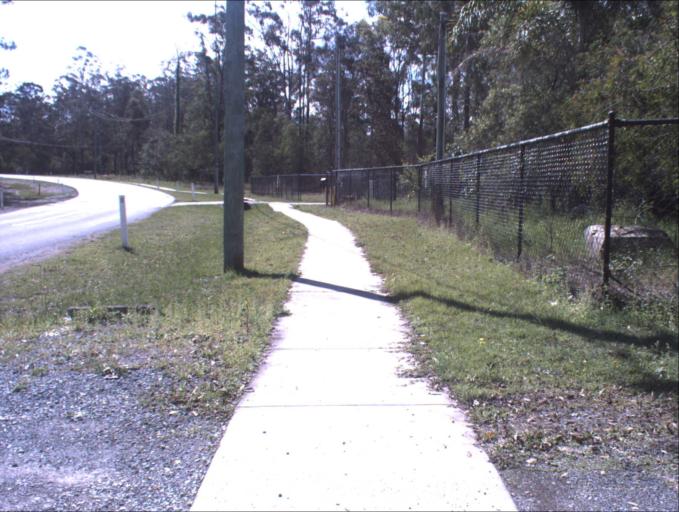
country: AU
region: Queensland
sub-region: Logan
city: Chambers Flat
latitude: -27.7452
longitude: 153.0539
